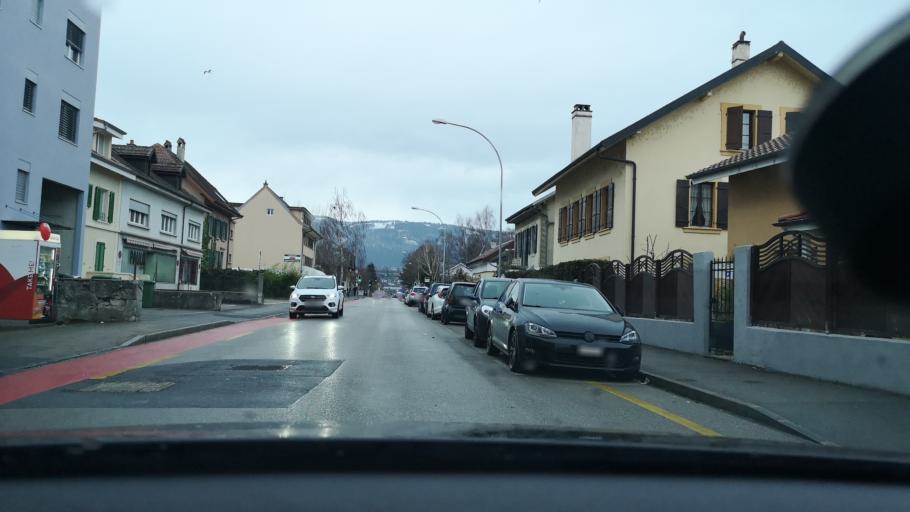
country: CH
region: Vaud
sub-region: Jura-Nord vaudois District
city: Yverdon-les-Bains
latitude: 46.7858
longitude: 6.6357
